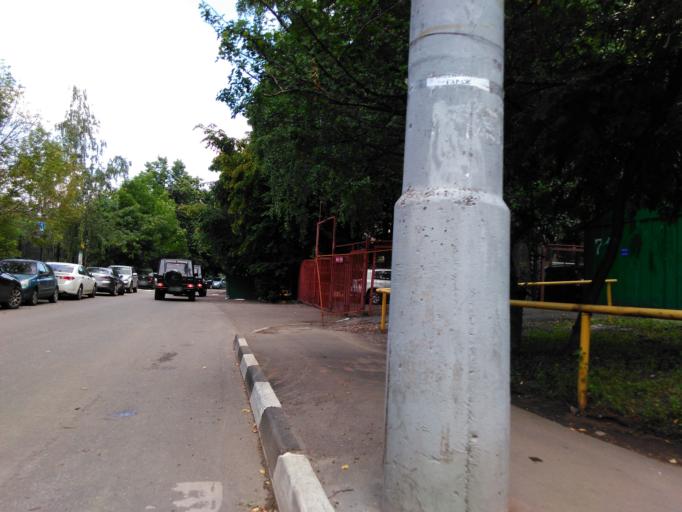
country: RU
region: Moskovskaya
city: Leninskiye Gory
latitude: 55.6993
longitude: 37.5517
